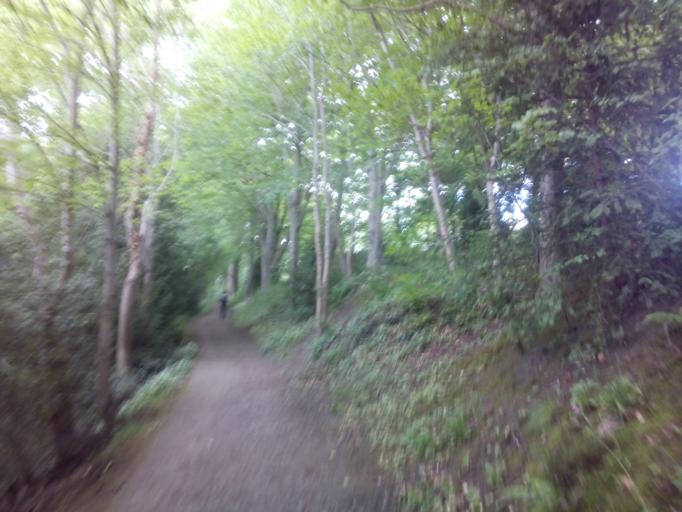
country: GB
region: England
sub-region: County Durham
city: Durham
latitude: 54.7703
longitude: -1.5752
